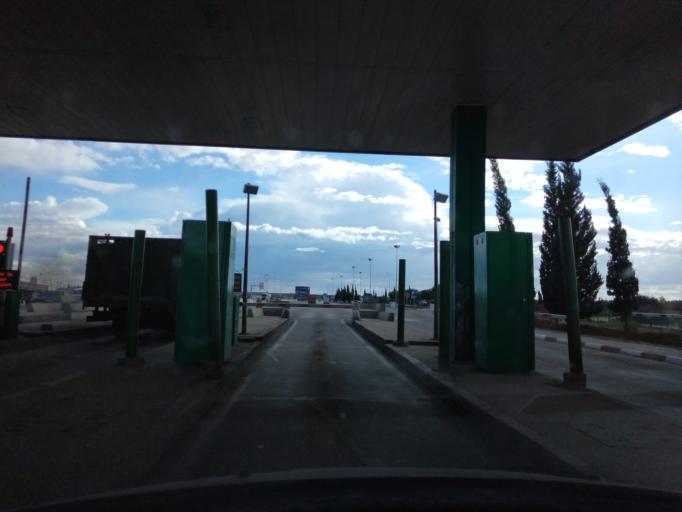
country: TN
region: Susah
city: Masakin
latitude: 35.6904
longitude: 10.5631
